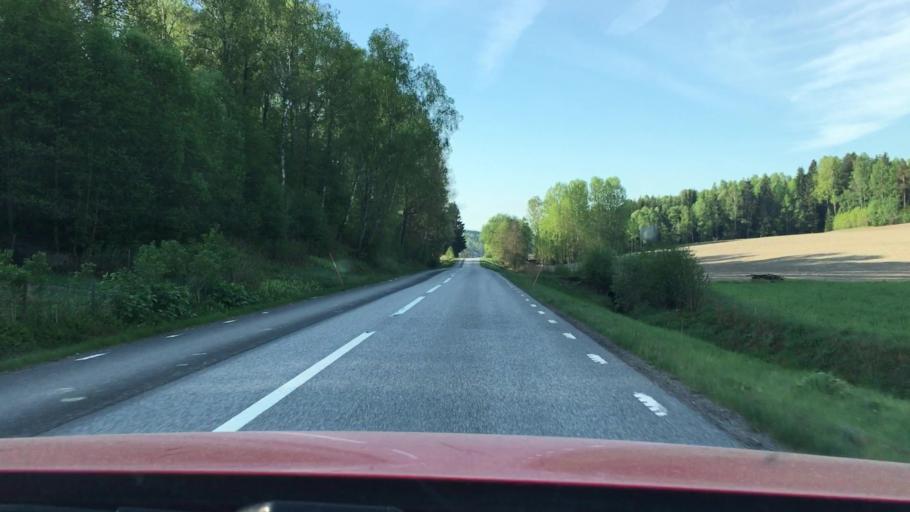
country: SE
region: Vaestra Goetaland
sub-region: Munkedals Kommun
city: Munkedal
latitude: 58.6171
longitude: 11.5585
